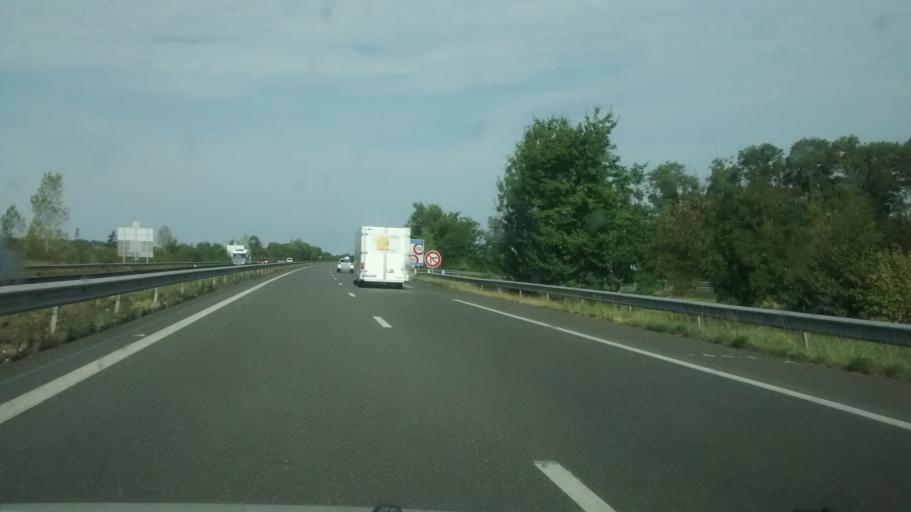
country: FR
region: Midi-Pyrenees
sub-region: Departement du Tarn-et-Garonne
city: Saint-Nicolas-de-la-Grave
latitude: 44.0442
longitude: 0.9973
